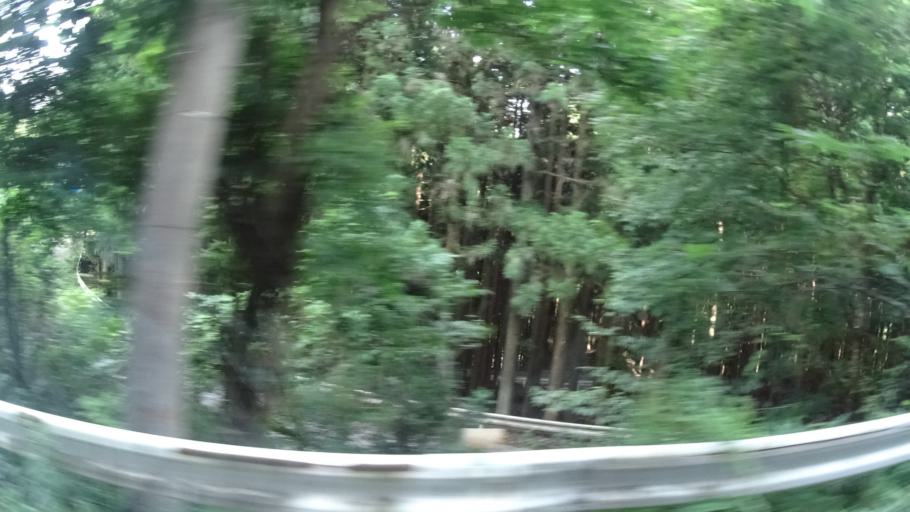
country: JP
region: Tochigi
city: Nikko
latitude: 36.7218
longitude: 139.5344
